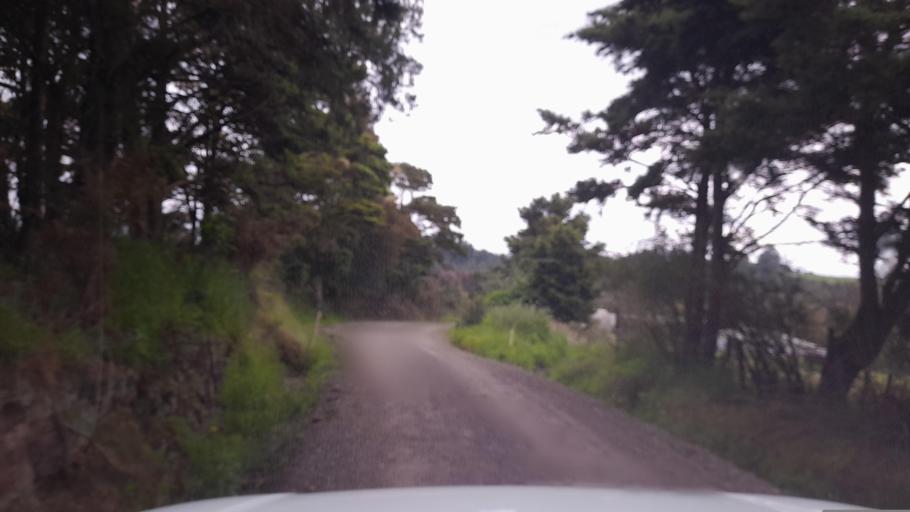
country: NZ
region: Northland
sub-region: Far North District
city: Waimate North
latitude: -35.3961
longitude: 173.7849
